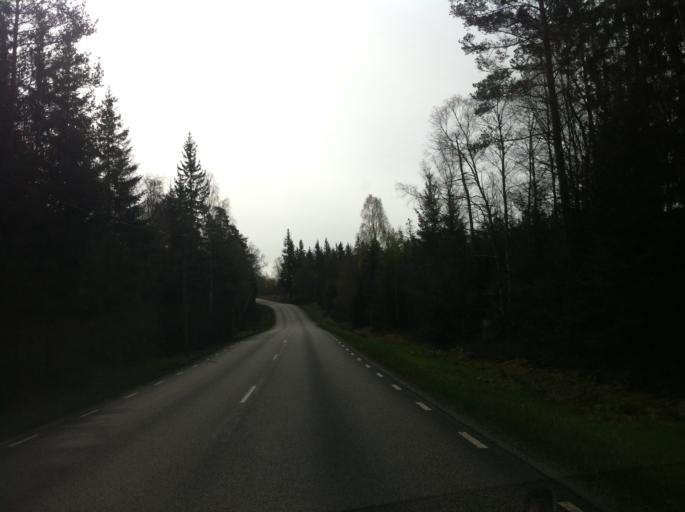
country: SE
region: Vaestra Goetaland
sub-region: Marks Kommun
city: Kinna
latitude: 57.4375
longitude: 12.7518
